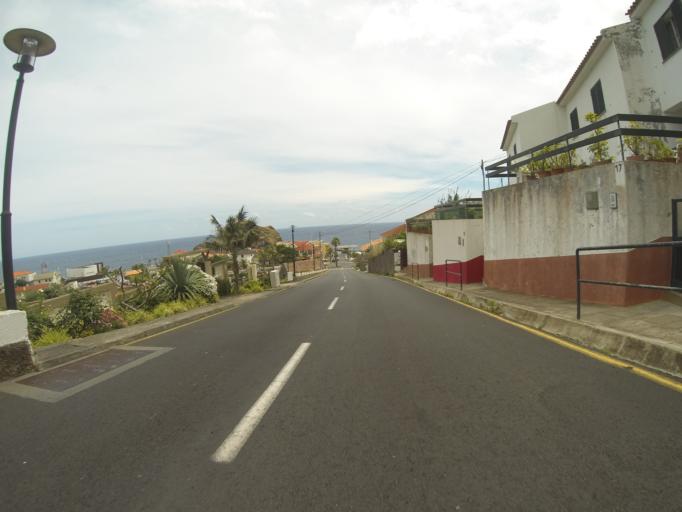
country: PT
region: Madeira
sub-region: Porto Moniz
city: Porto Moniz
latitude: 32.8635
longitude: -17.1655
